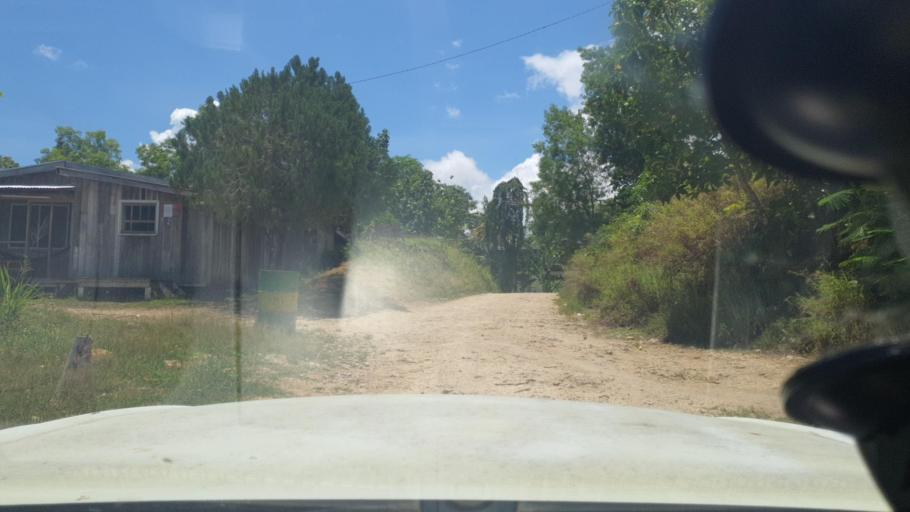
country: SB
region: Guadalcanal
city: Honiara
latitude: -9.4322
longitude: 159.9320
